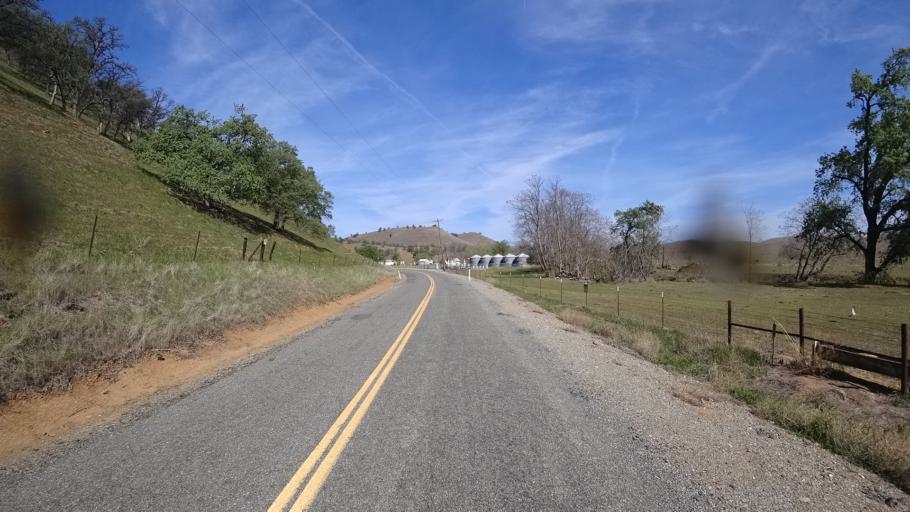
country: US
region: California
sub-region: Glenn County
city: Willows
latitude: 39.5460
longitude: -122.3981
